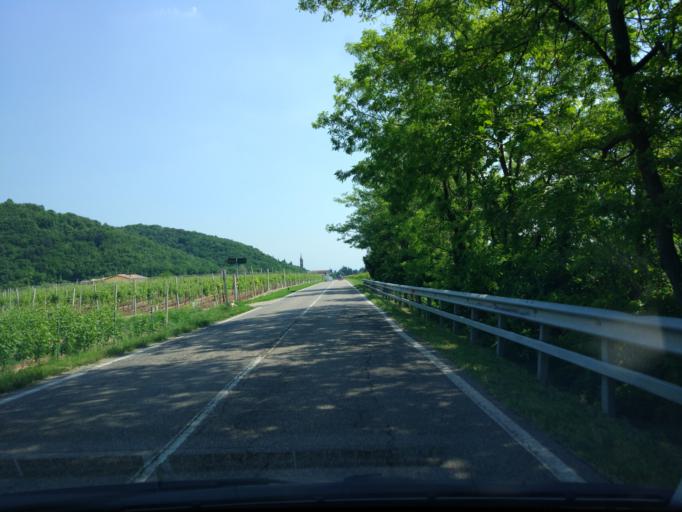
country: IT
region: Veneto
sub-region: Provincia di Verona
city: Tregnago
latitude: 45.5311
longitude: 11.1599
